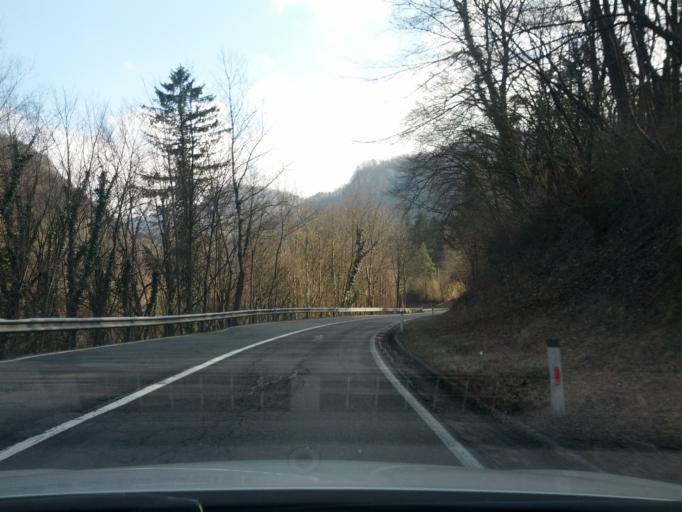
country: SI
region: Zagorje ob Savi
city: Kisovec
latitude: 46.0906
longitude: 14.9405
